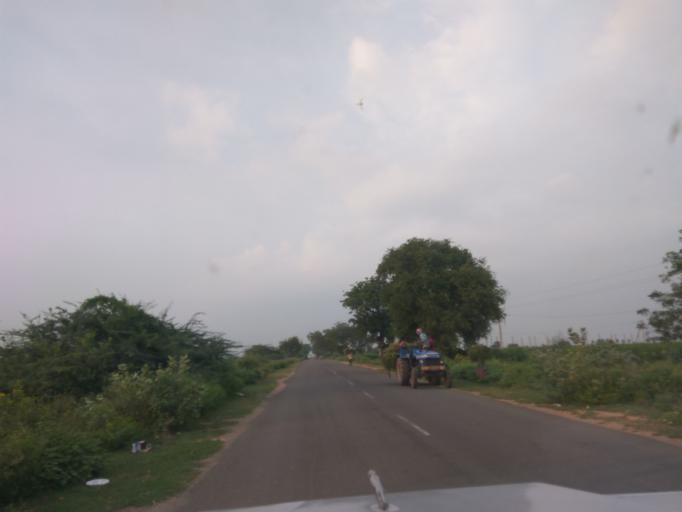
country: IN
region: Andhra Pradesh
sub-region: Guntur
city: Vinukonda
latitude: 16.0941
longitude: 79.7491
